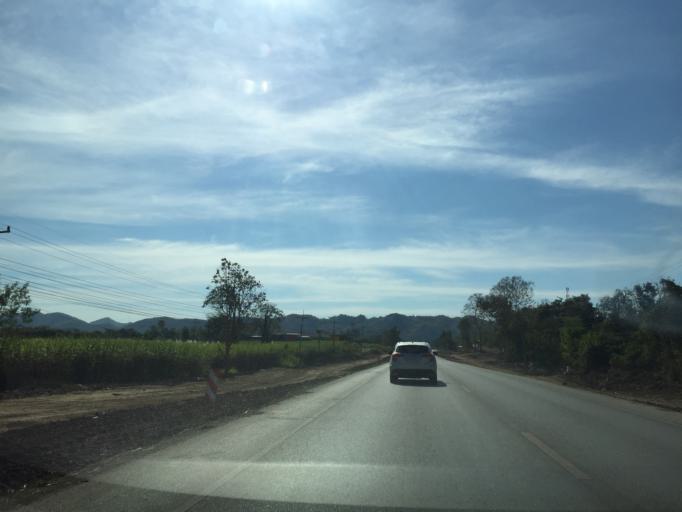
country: TH
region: Loei
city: Wang Saphung
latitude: 17.2966
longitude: 101.8535
